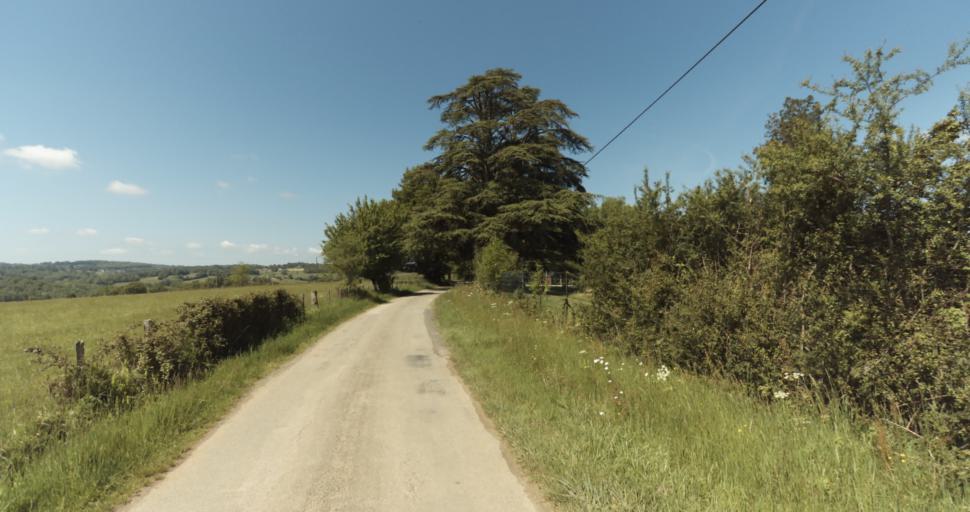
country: FR
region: Limousin
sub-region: Departement de la Haute-Vienne
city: Le Vigen
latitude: 45.7556
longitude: 1.3022
